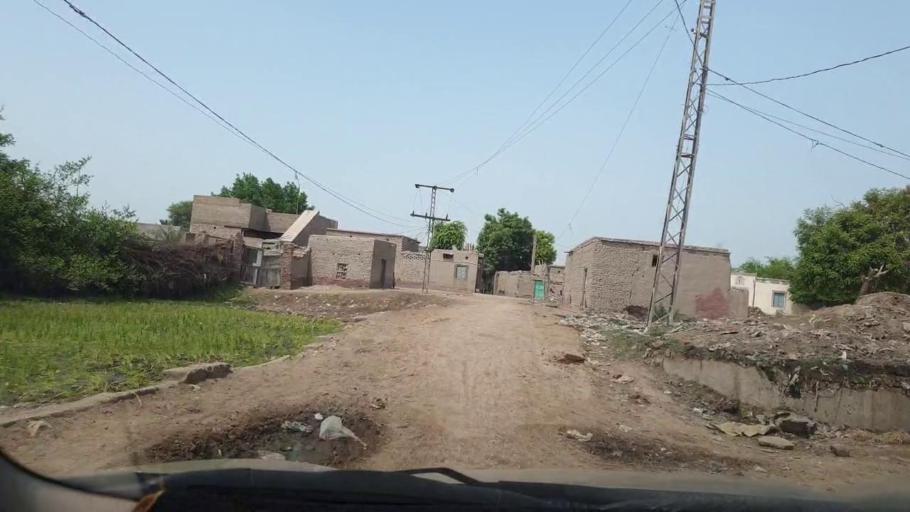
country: PK
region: Sindh
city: Larkana
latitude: 27.5883
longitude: 68.1457
